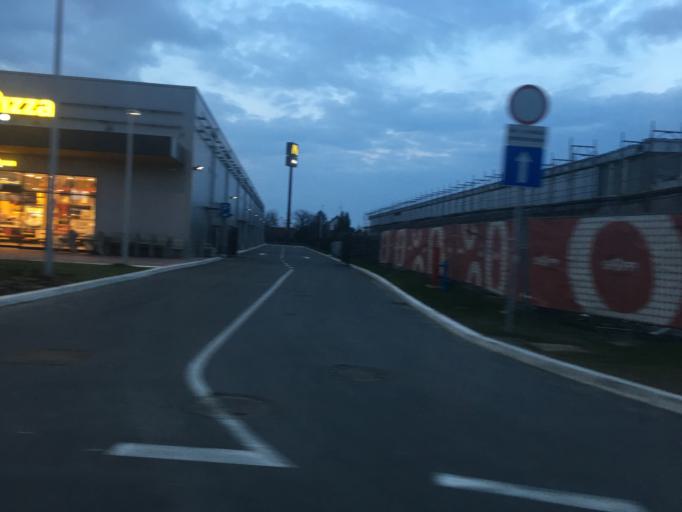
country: RS
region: Central Serbia
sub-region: Belgrade
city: Stari Grad
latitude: 44.8875
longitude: 20.4587
